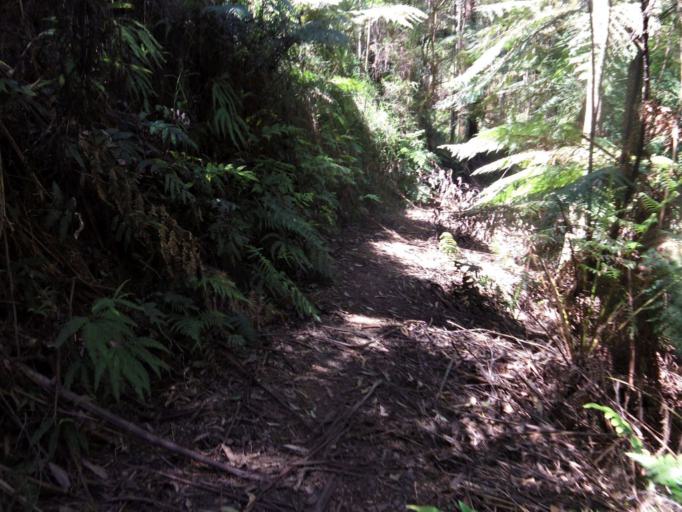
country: AU
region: Victoria
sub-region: Yarra Ranges
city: Millgrove
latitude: -37.8600
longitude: 145.7627
